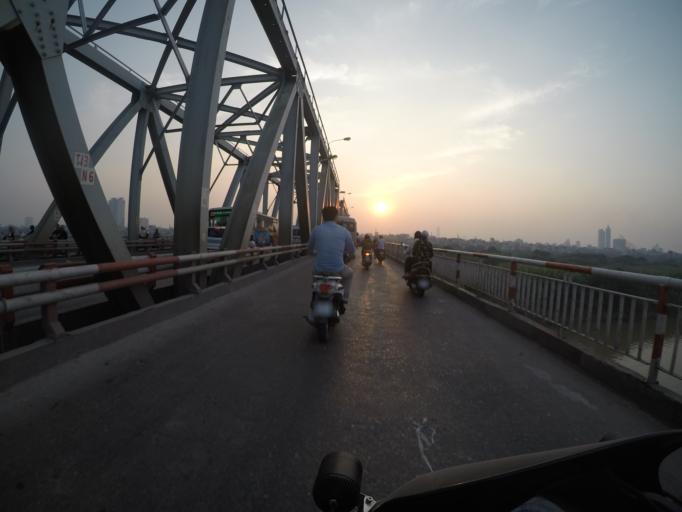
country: VN
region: Ha Noi
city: Hoan Kiem
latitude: 21.0381
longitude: 105.8613
